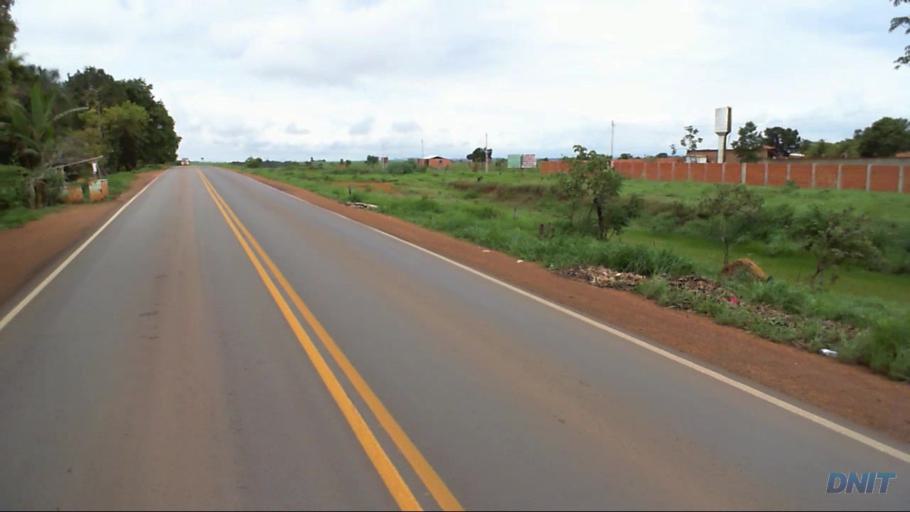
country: BR
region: Goias
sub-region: Padre Bernardo
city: Padre Bernardo
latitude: -15.3597
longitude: -48.2259
